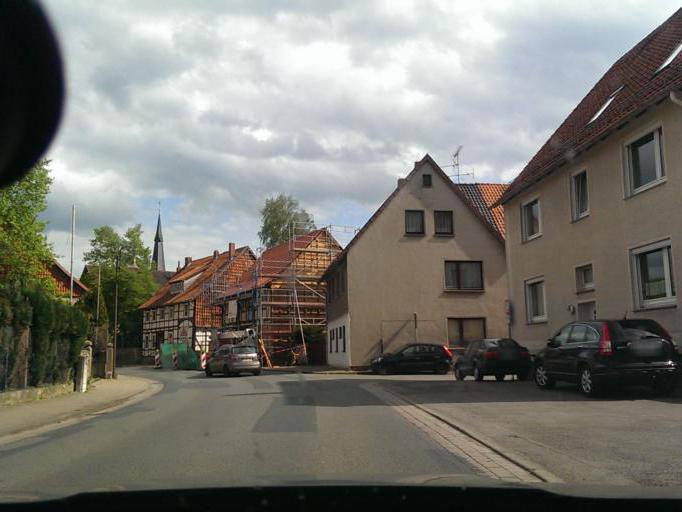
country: DE
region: Lower Saxony
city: Eime
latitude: 52.0787
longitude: 9.7218
